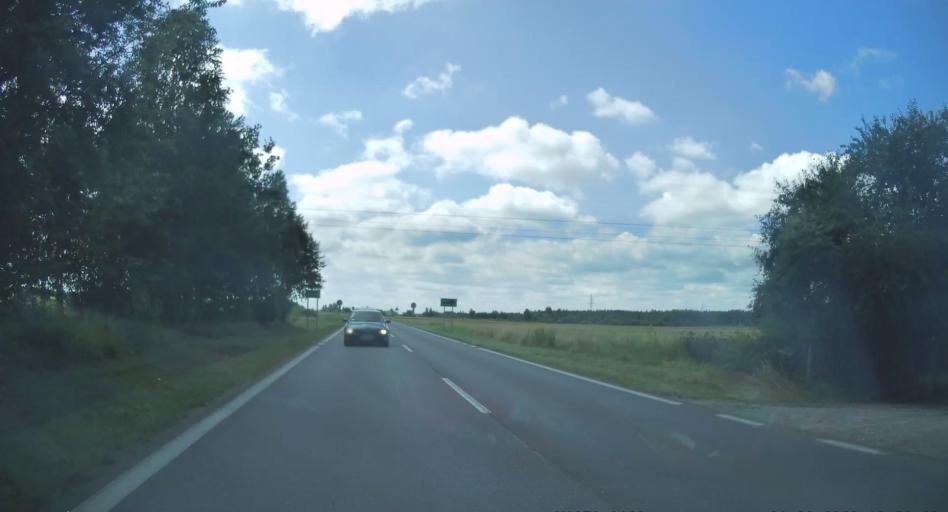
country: PL
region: Subcarpathian Voivodeship
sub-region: Powiat mielecki
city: Padew Narodowa
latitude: 50.3968
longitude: 21.4651
